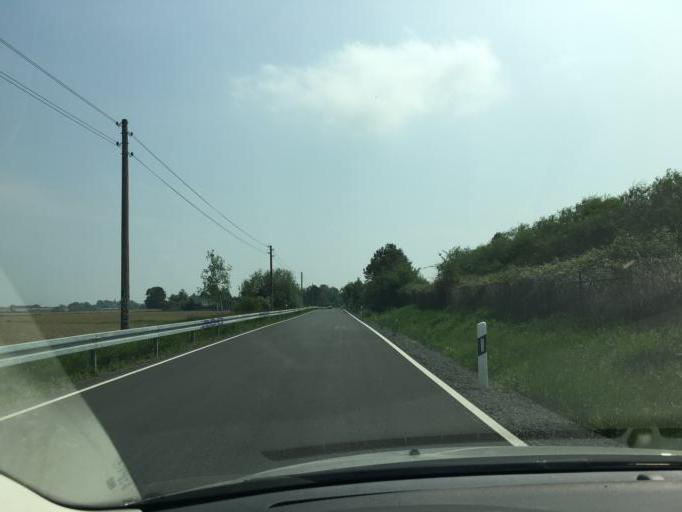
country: DE
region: Saxony
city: Grossposna
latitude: 51.2946
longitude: 12.4976
